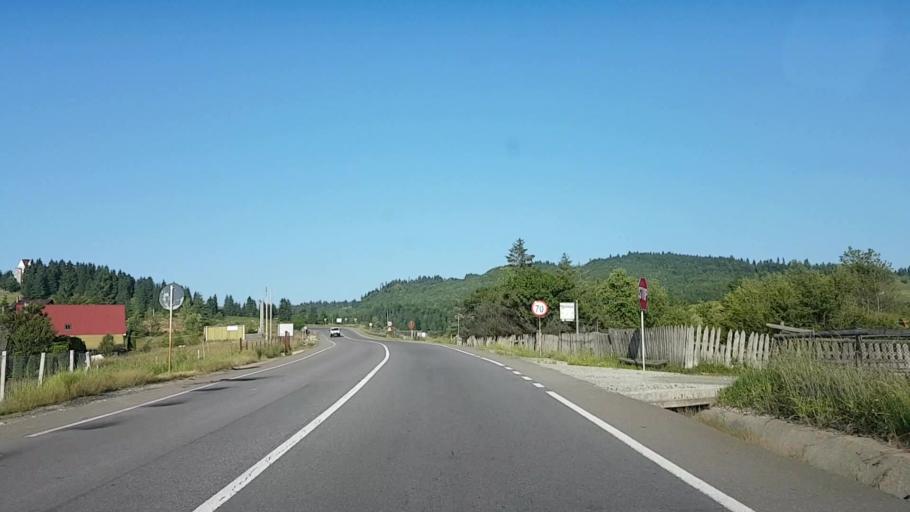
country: RO
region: Bistrita-Nasaud
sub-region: Comuna Lunca Ilvei
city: Lunca Ilvei
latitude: 47.2328
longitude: 24.9938
